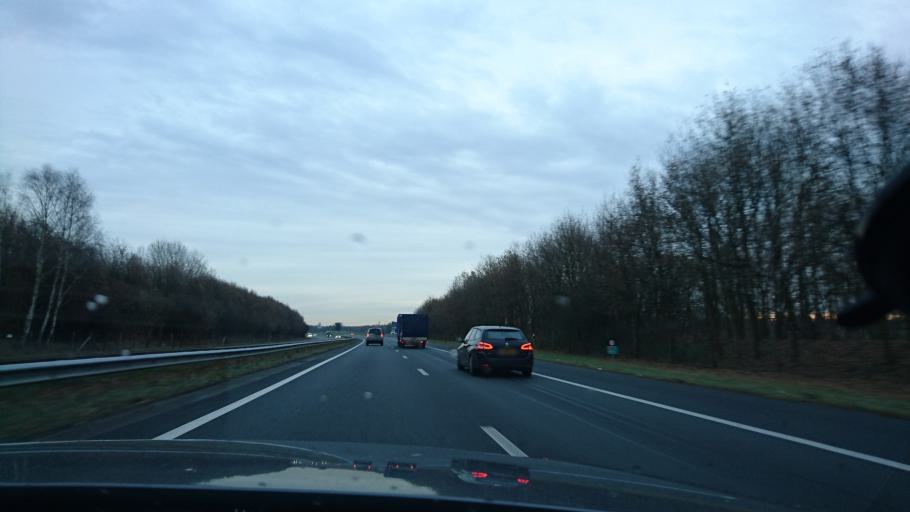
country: NL
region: Overijssel
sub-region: Gemeente Oldenzaal
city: Oldenzaal
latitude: 52.2898
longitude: 6.9161
